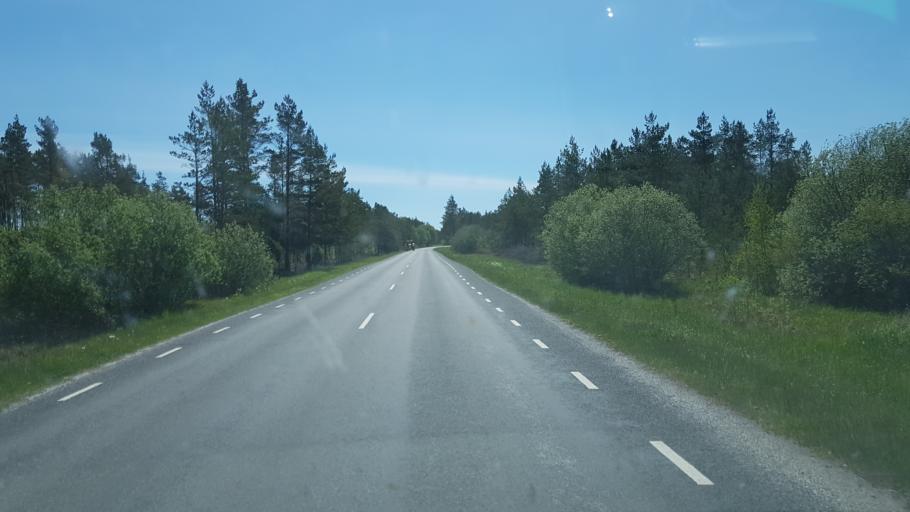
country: EE
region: Saare
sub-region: Kuressaare linn
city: Kuressaare
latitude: 58.3236
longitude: 22.4630
